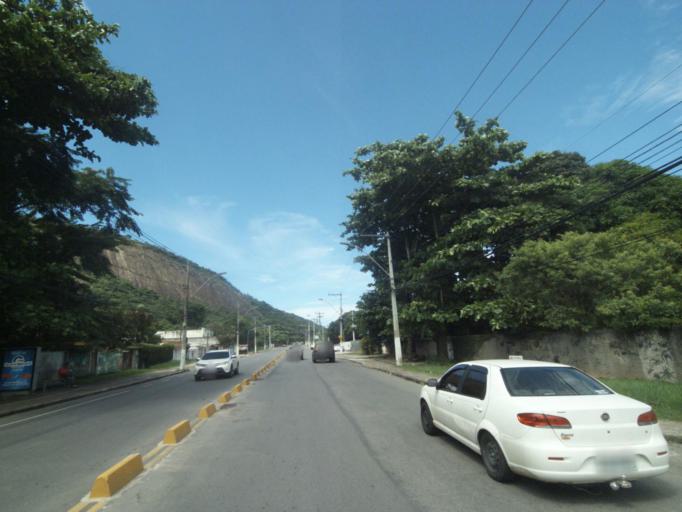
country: BR
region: Rio de Janeiro
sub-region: Niteroi
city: Niteroi
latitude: -22.9552
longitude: -43.0281
